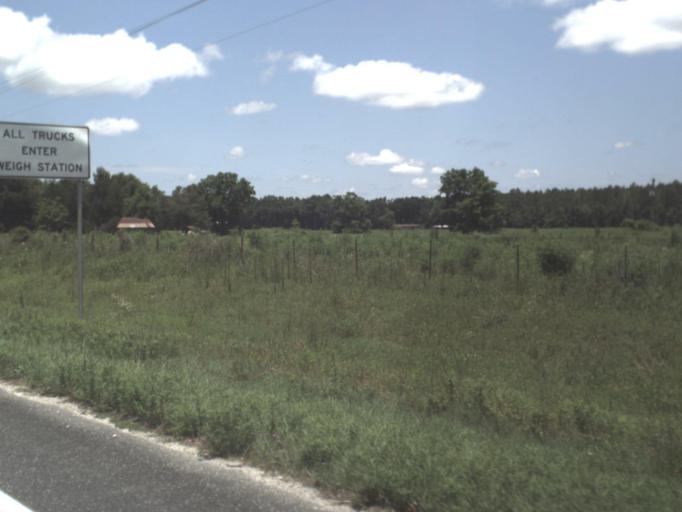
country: US
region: Florida
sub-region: Suwannee County
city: Wellborn
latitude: 29.9524
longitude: -82.8549
